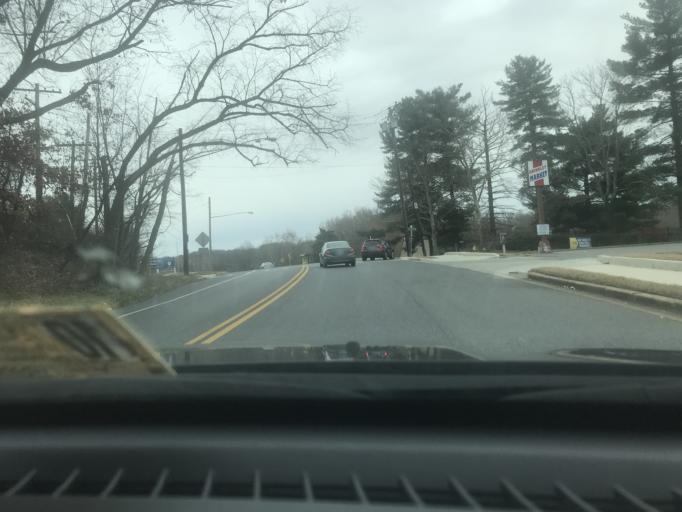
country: US
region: Maryland
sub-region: Prince George's County
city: Temple Hills
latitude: 38.8035
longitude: -76.9511
